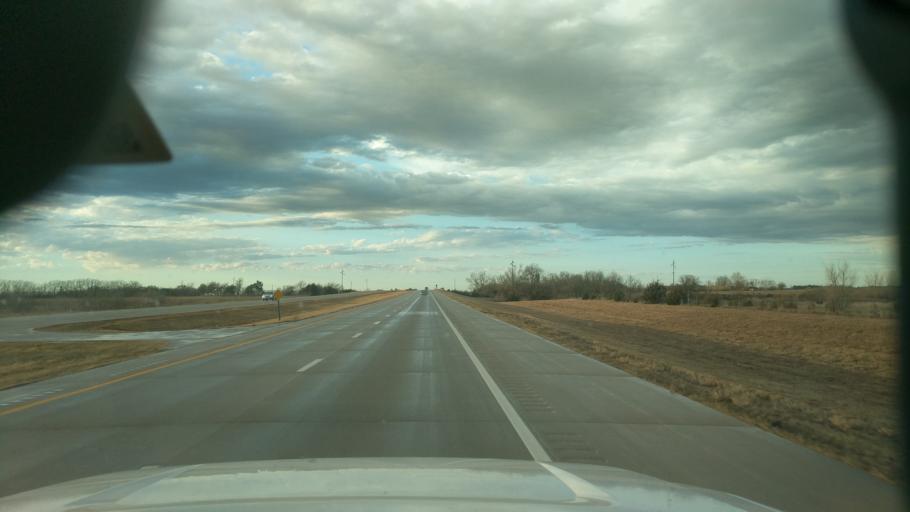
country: US
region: Kansas
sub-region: Harvey County
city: Hesston
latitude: 38.1125
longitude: -97.3842
